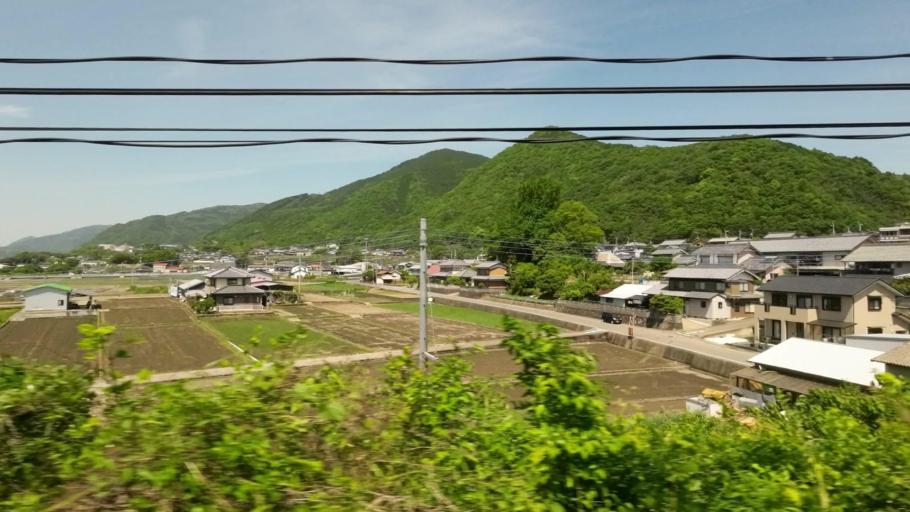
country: JP
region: Tokushima
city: Ikedacho
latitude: 34.0405
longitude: 133.8666
